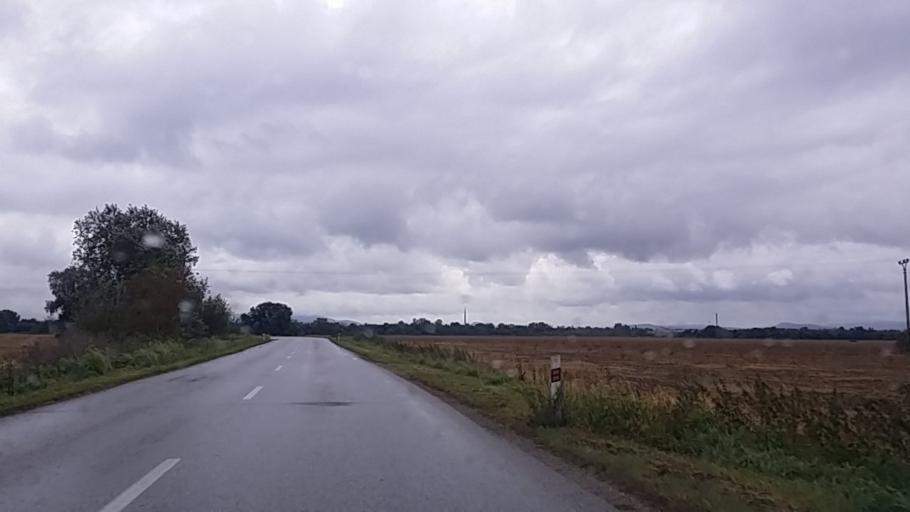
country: SK
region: Nitriansky
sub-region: Okres Nove Zamky
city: Sturovo
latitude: 47.8241
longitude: 18.7183
